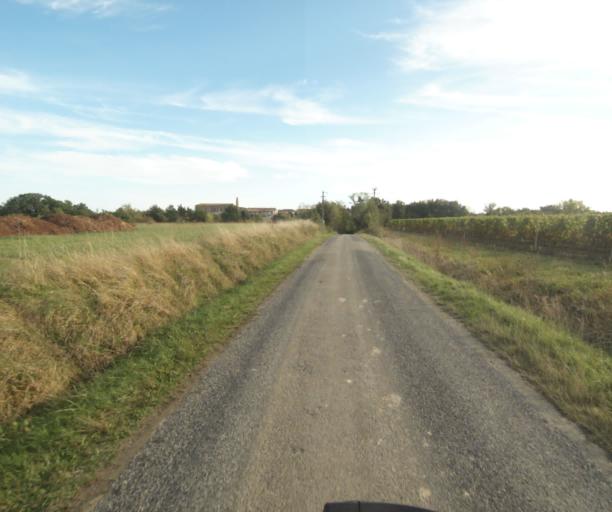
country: FR
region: Midi-Pyrenees
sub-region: Departement du Tarn-et-Garonne
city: Finhan
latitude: 43.9037
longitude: 1.1333
